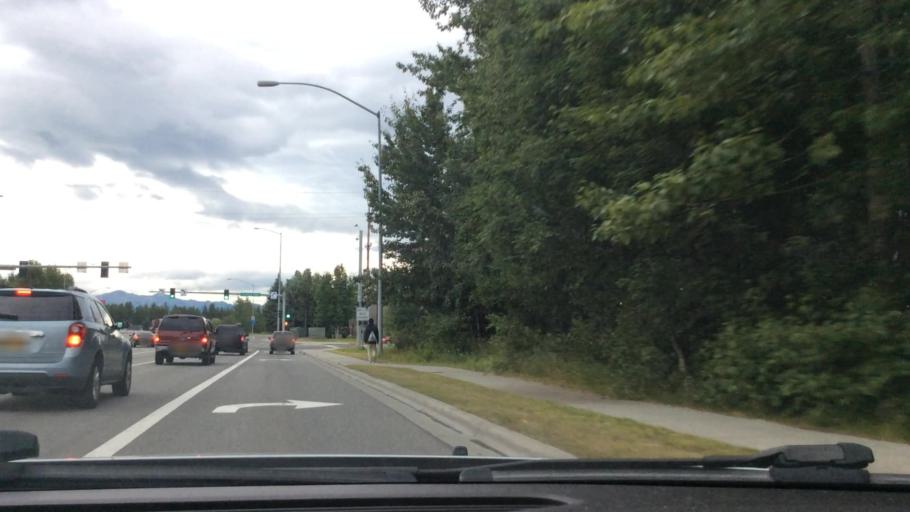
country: US
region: Alaska
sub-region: Anchorage Municipality
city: Anchorage
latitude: 61.1674
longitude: -149.8384
